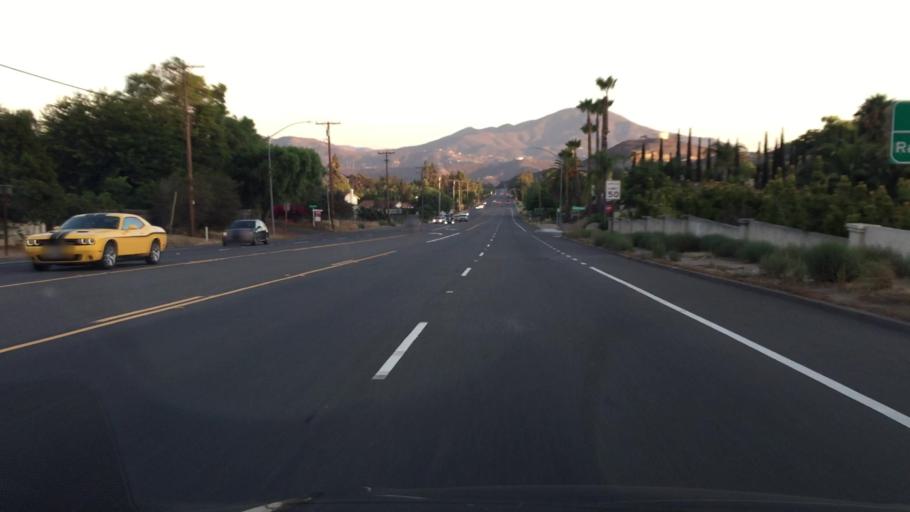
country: US
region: California
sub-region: San Diego County
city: Rancho San Diego
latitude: 32.7752
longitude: -116.9280
